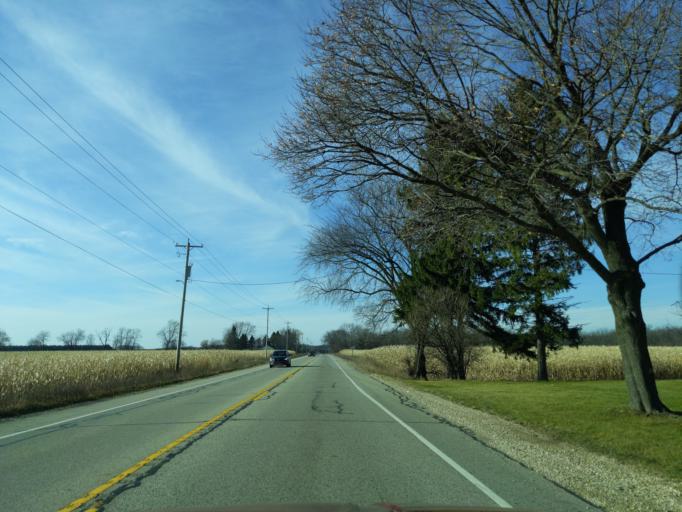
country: US
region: Wisconsin
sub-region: Jefferson County
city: Palmyra
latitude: 42.7961
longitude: -88.6280
